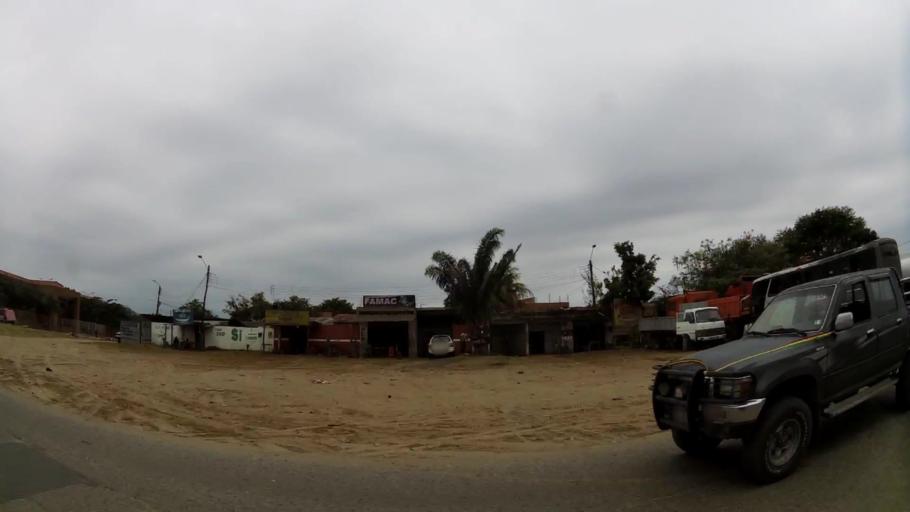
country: BO
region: Santa Cruz
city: Santa Cruz de la Sierra
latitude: -17.8238
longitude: -63.2045
